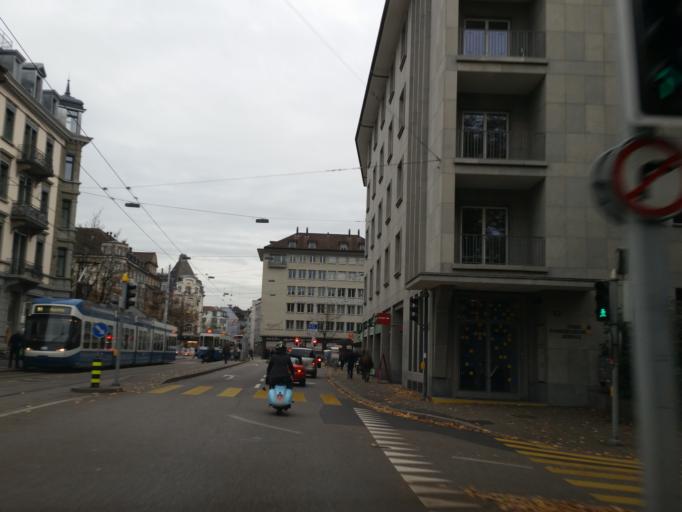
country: CH
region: Zurich
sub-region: Bezirk Zuerich
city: Zurich
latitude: 47.3652
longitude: 8.5531
